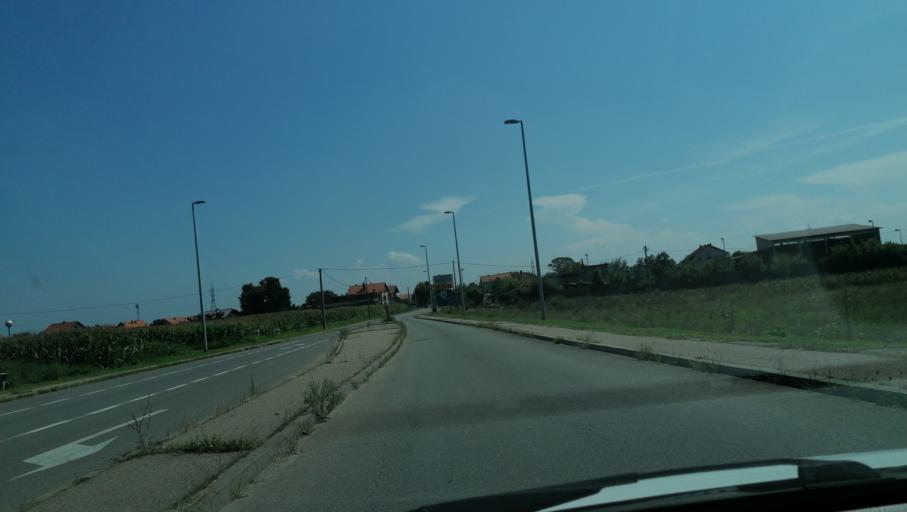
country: BA
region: Republika Srpska
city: Bijeljina
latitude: 44.7739
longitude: 19.2010
